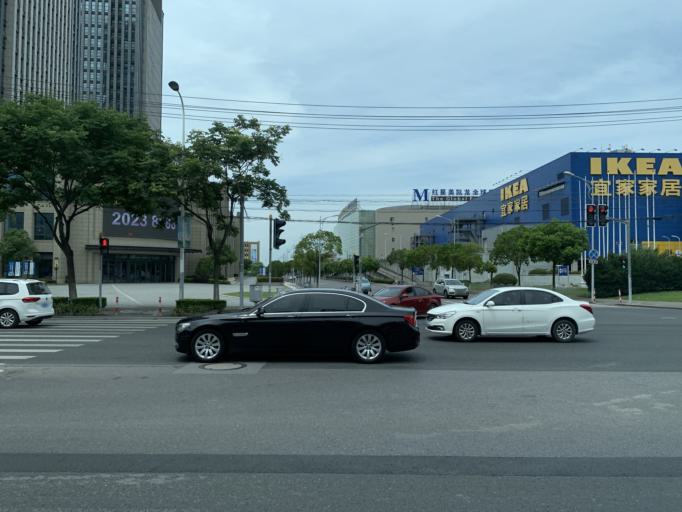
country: CN
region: Shanghai Shi
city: Kangqiao
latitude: 31.1612
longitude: 121.5597
